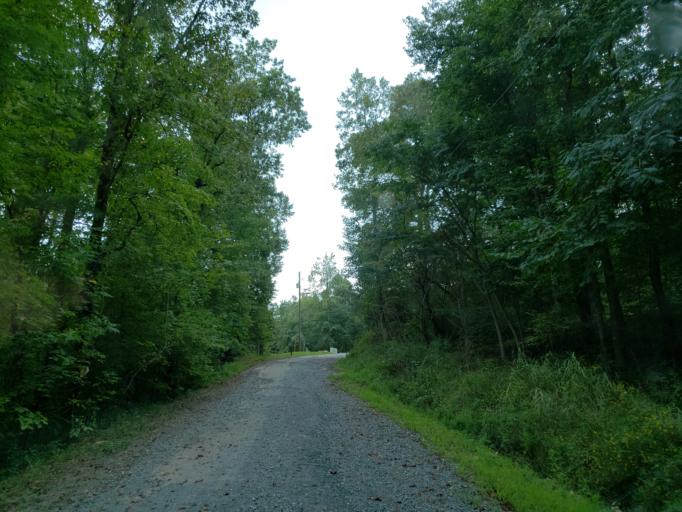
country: US
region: Georgia
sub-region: Pickens County
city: Jasper
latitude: 34.5511
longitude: -84.5154
